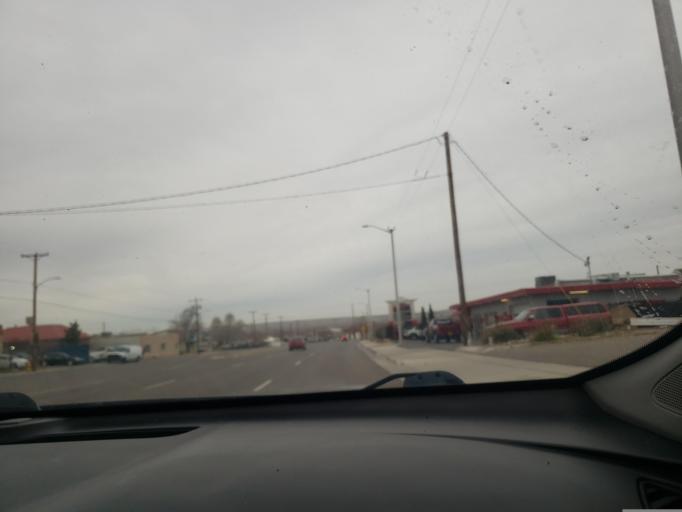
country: US
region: New Mexico
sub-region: Bernalillo County
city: Albuquerque
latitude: 35.0602
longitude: -106.6403
